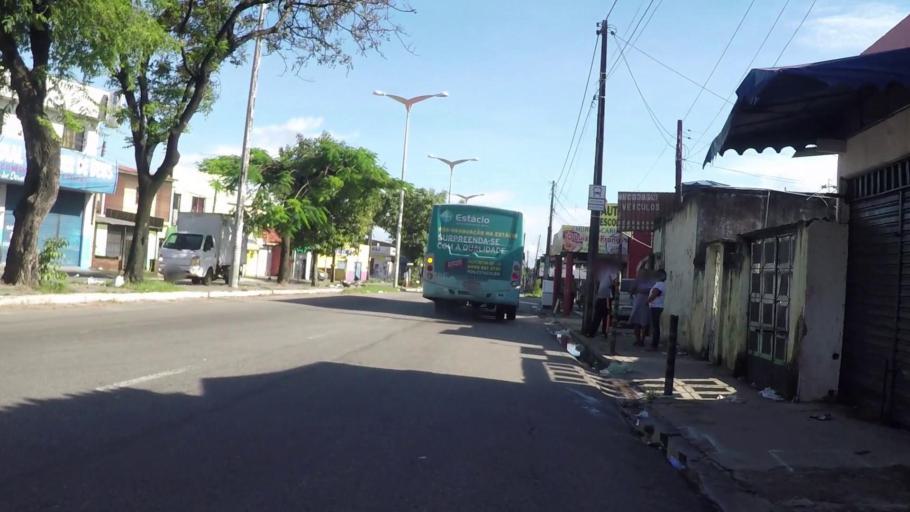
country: BR
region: Ceara
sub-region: Fortaleza
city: Fortaleza
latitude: -3.7261
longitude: -38.5855
